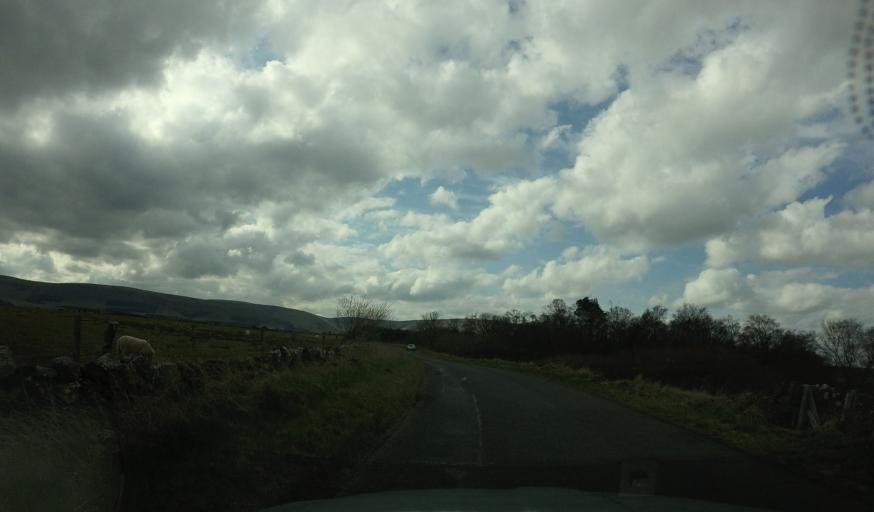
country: GB
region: Scotland
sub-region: Midlothian
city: Bonnyrigg
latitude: 55.7814
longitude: -3.1312
